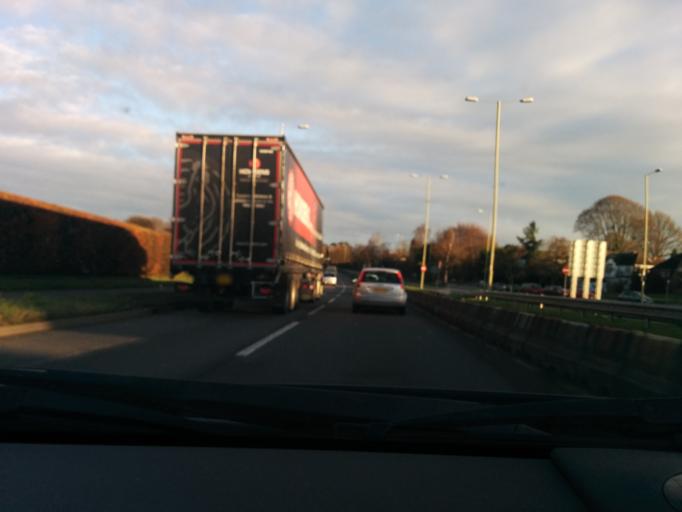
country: GB
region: England
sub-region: Oxfordshire
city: Cowley
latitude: 51.7627
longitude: -1.1927
